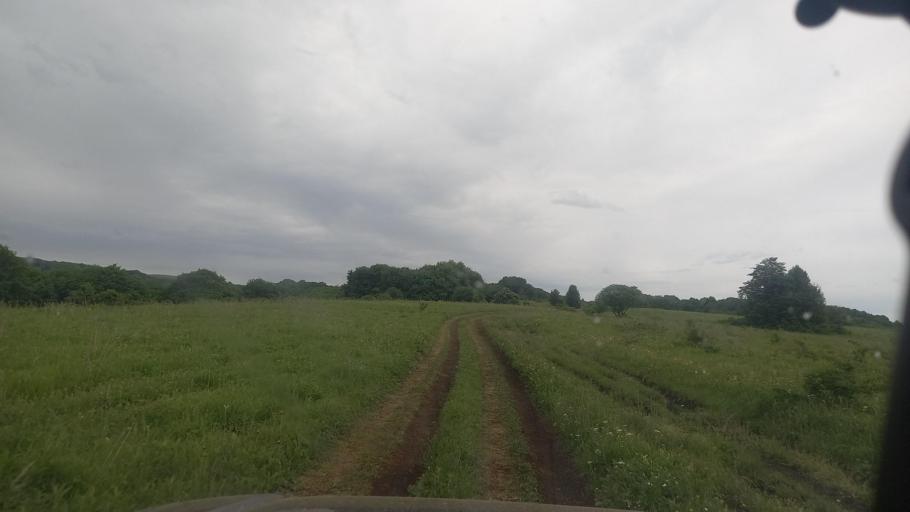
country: RU
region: Karachayevo-Cherkesiya
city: Pregradnaya
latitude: 44.0209
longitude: 41.2897
